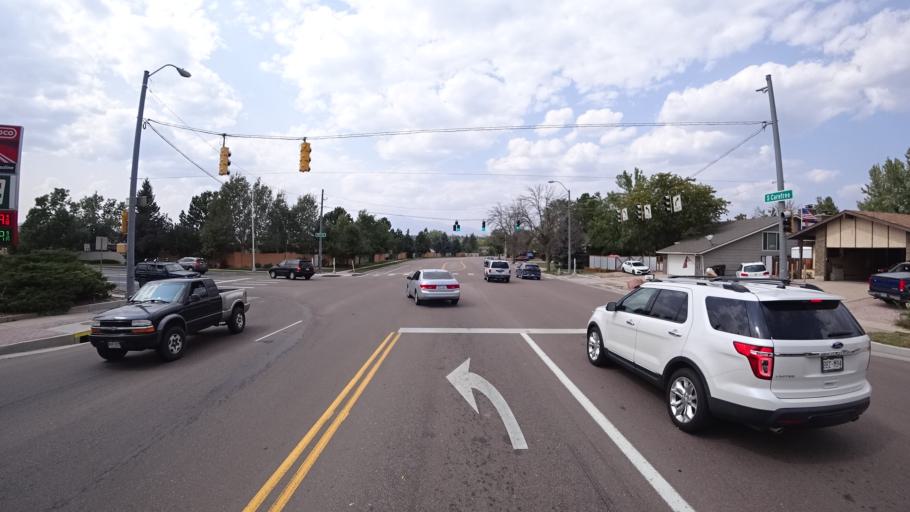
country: US
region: Colorado
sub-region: El Paso County
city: Cimarron Hills
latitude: 38.8740
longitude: -104.7476
